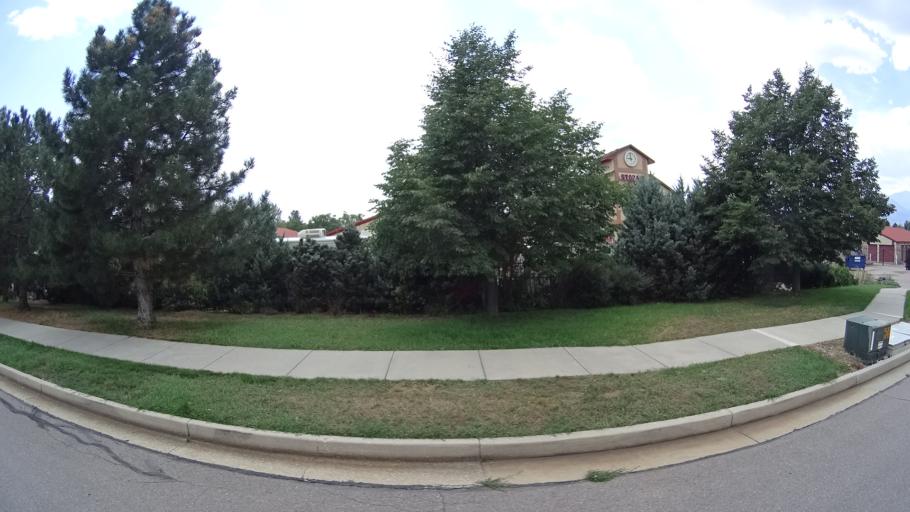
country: US
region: Colorado
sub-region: El Paso County
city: Cimarron Hills
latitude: 38.8344
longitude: -104.7473
